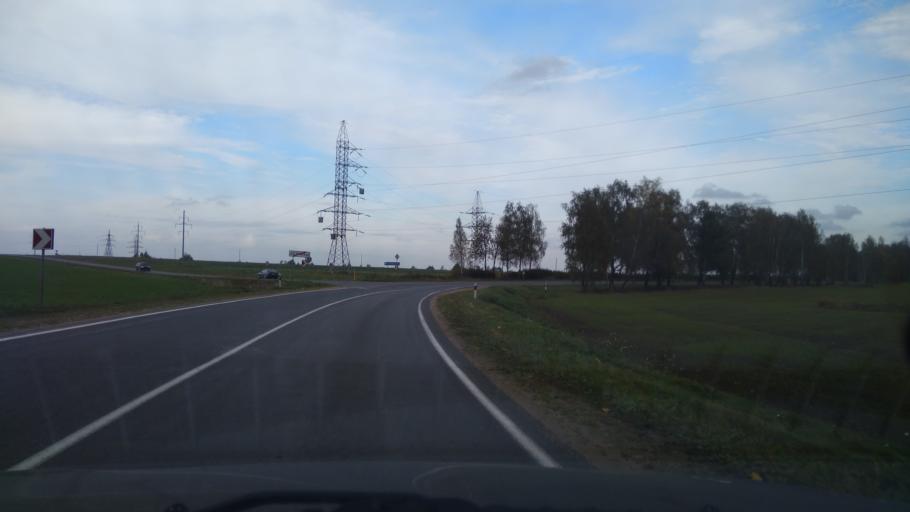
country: BY
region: Minsk
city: Rudzyensk
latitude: 53.6176
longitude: 27.8542
